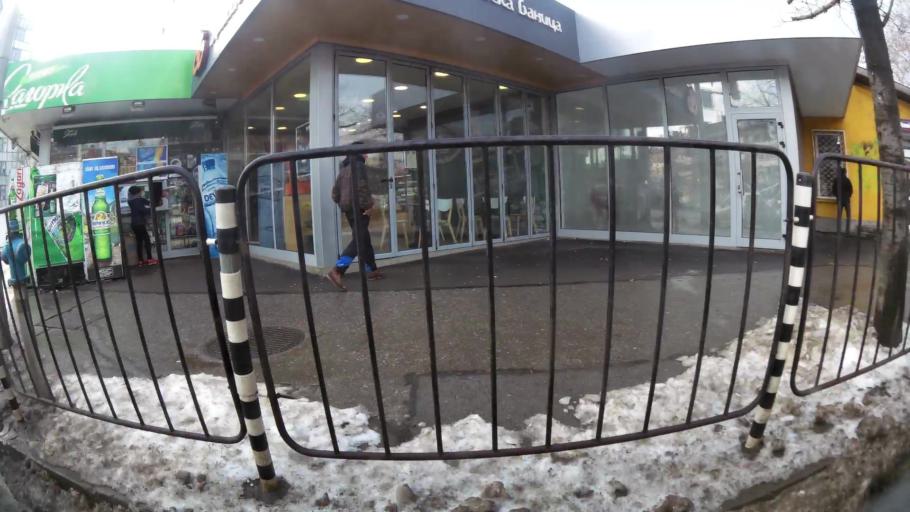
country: BG
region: Sofia-Capital
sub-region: Stolichna Obshtina
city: Sofia
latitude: 42.7012
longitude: 23.2920
